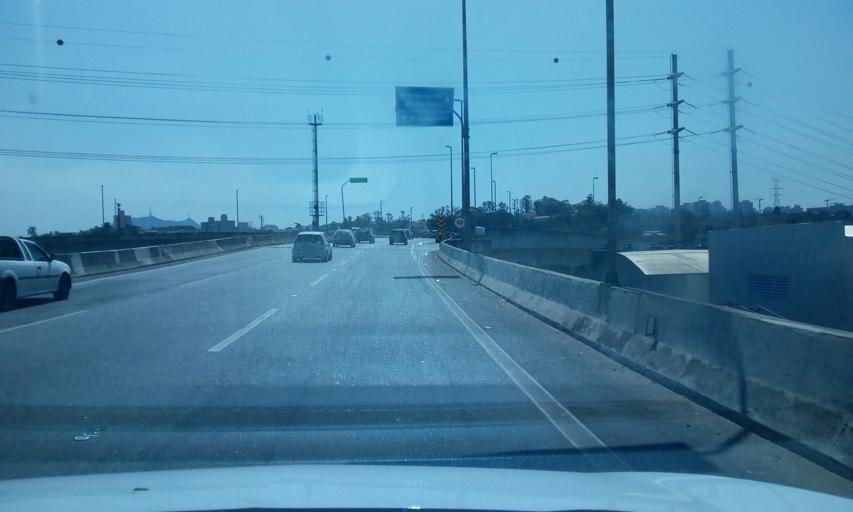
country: BR
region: Sao Paulo
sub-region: Osasco
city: Osasco
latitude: -23.5166
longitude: -46.7257
